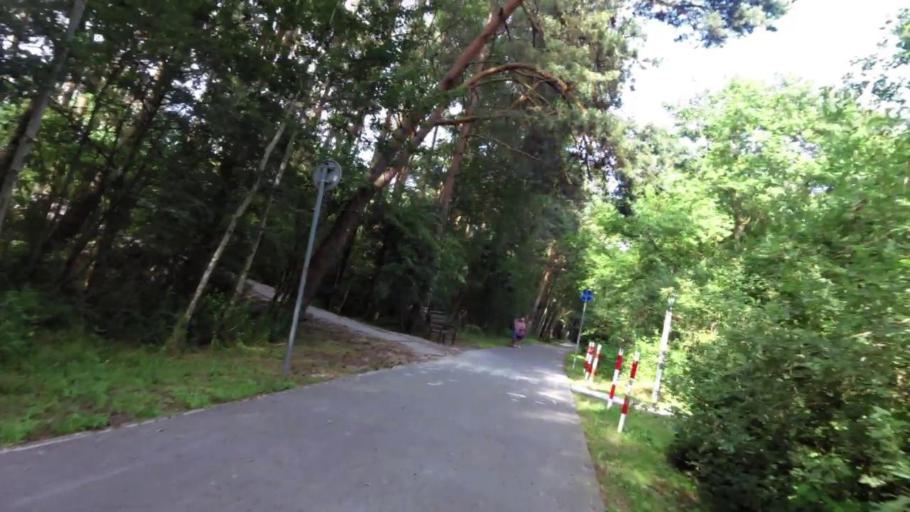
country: PL
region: West Pomeranian Voivodeship
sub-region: Powiat kolobrzeski
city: Grzybowo
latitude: 54.1666
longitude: 15.4929
